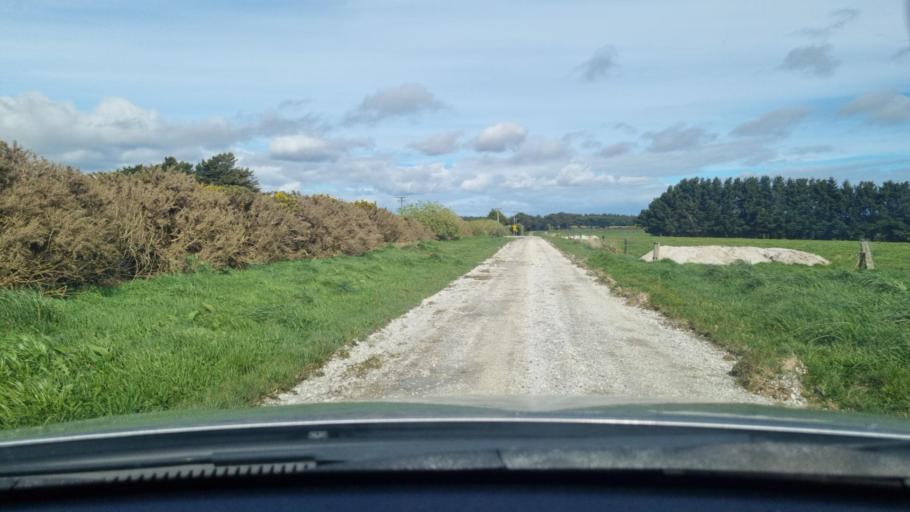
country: NZ
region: Southland
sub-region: Invercargill City
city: Invercargill
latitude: -46.4570
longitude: 168.3869
